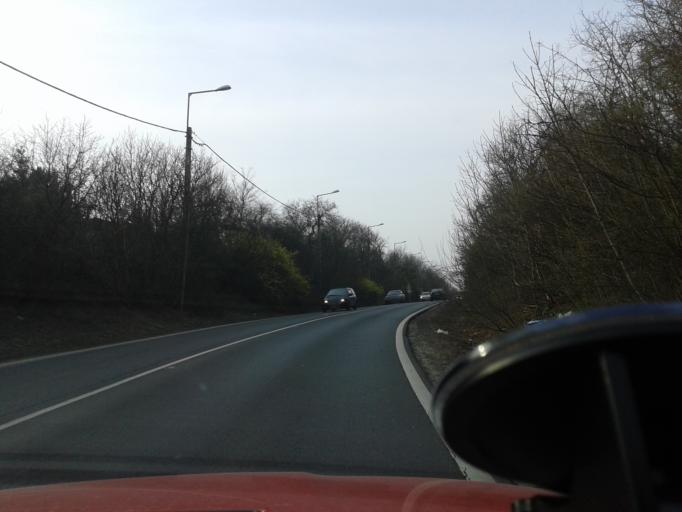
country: HU
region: Budapest
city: Budapest XXII. keruelet
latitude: 47.4393
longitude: 19.0084
